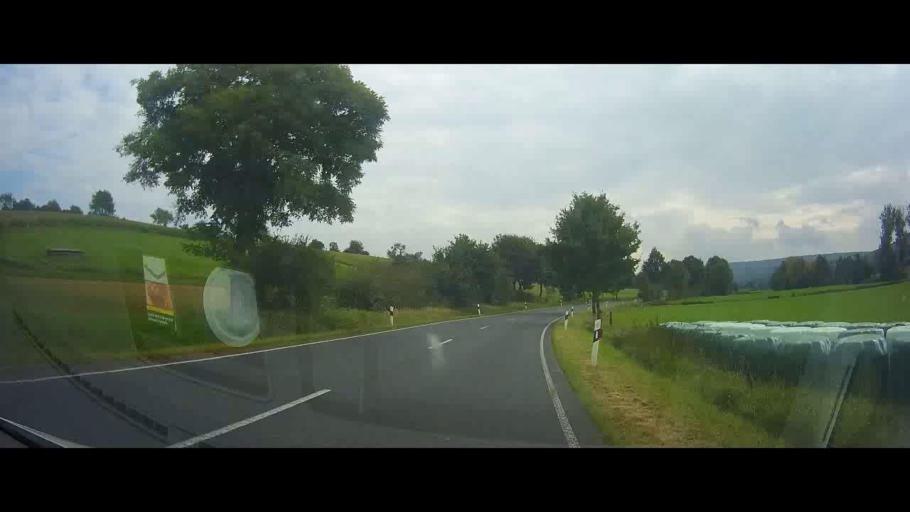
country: DE
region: Lower Saxony
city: Uslar
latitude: 51.6107
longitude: 9.6731
